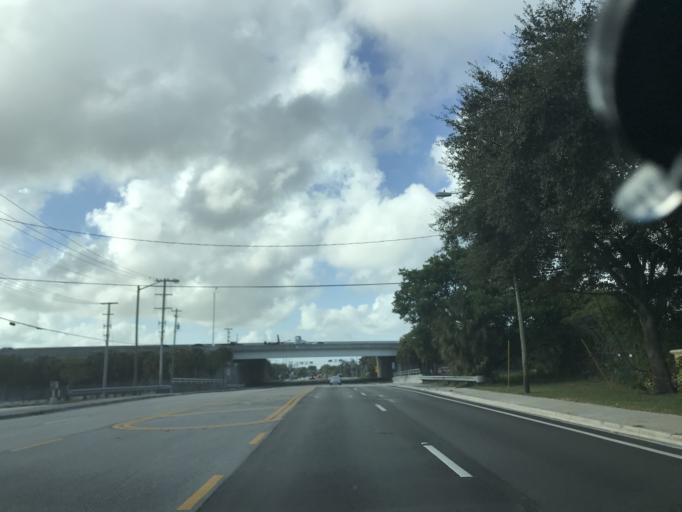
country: US
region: Florida
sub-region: Palm Beach County
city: Delray Beach
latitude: 26.4708
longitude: -80.0877
